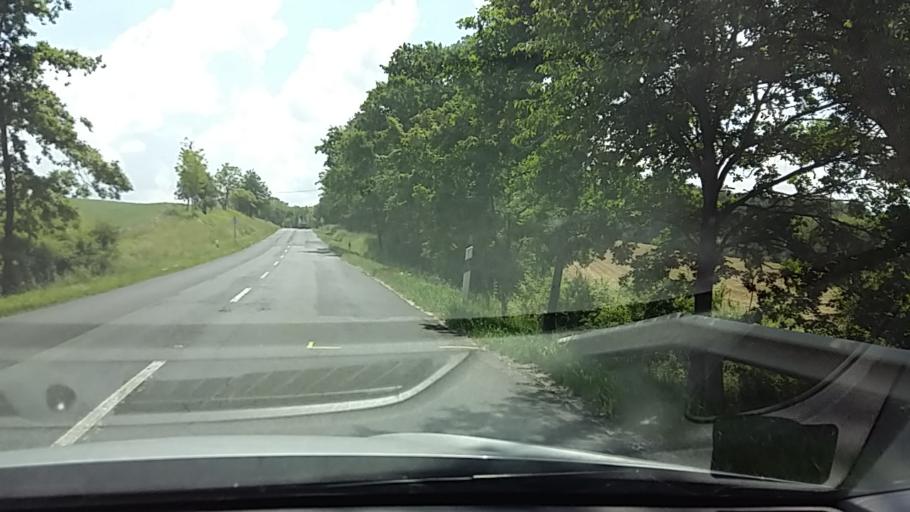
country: HU
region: Zala
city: Zalalovo
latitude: 46.9011
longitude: 16.7047
